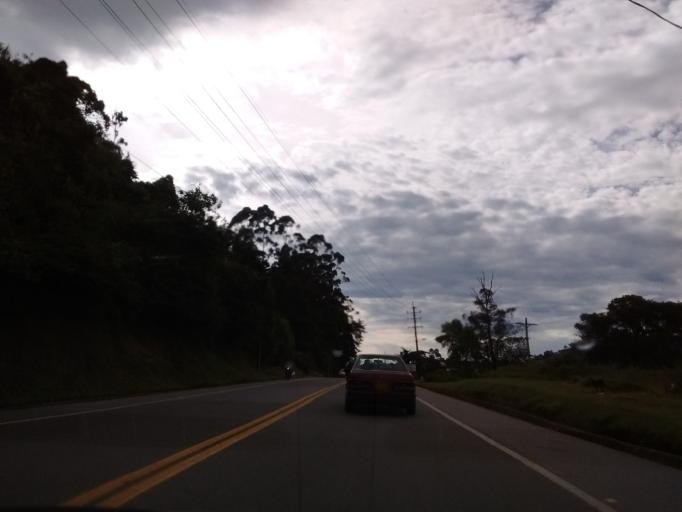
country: CO
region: Antioquia
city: Santuario
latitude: 6.1320
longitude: -75.2597
